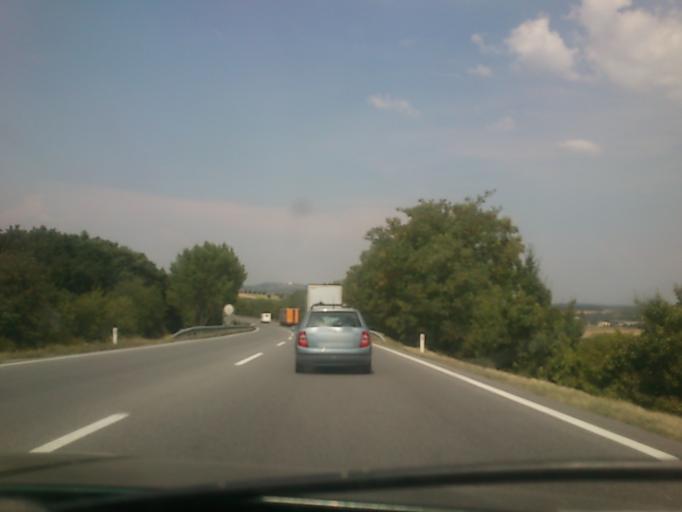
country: AT
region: Lower Austria
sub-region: Politischer Bezirk Mistelbach
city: Drasenhofen
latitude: 48.7406
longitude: 16.6576
